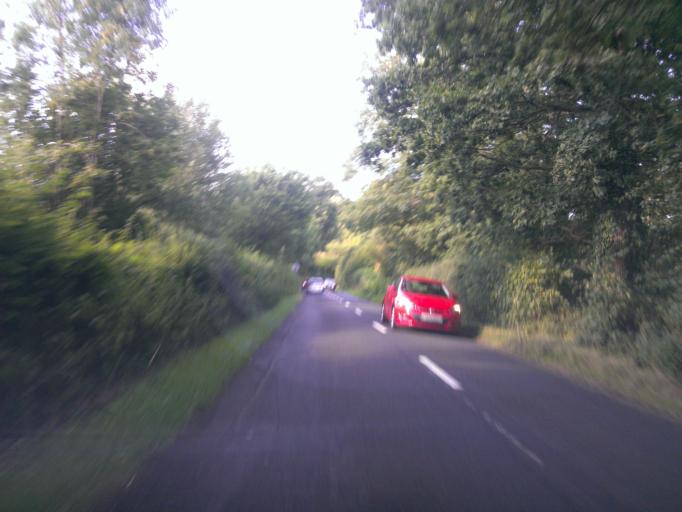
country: GB
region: England
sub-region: Kent
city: Edenbridge
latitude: 51.2009
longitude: 0.1218
